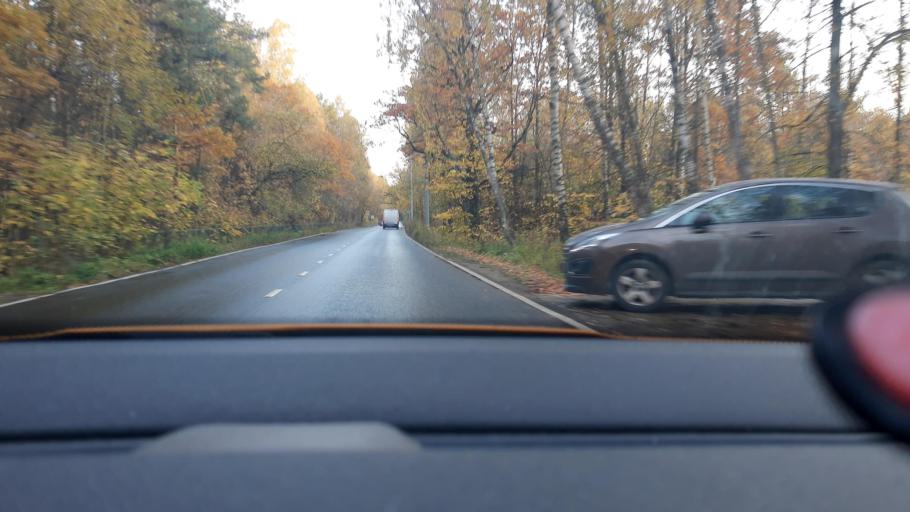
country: RU
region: Moskovskaya
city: Bogorodskoye
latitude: 55.8297
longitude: 37.7463
